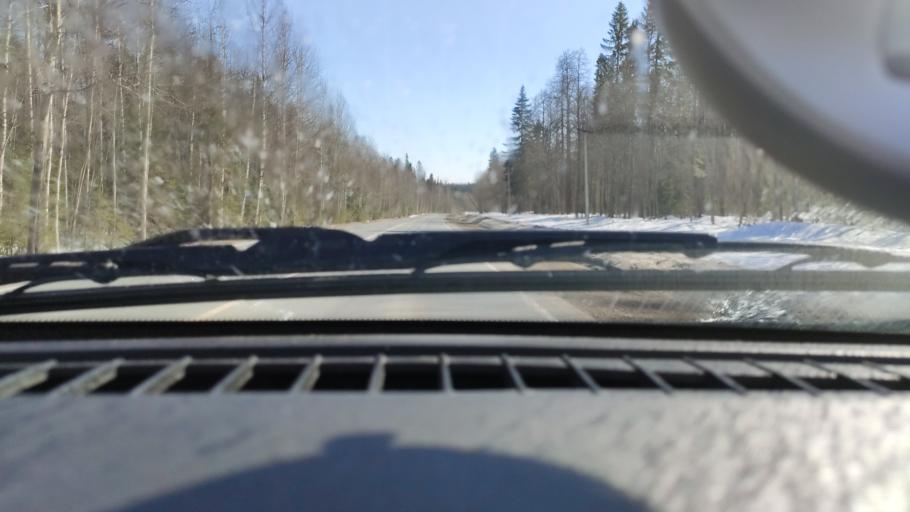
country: RU
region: Perm
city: Perm
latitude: 58.2091
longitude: 56.1914
